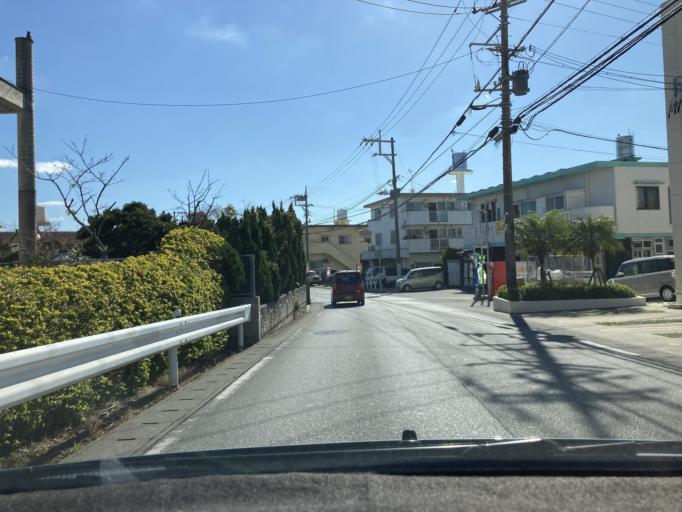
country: JP
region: Okinawa
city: Okinawa
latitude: 26.3522
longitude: 127.8246
